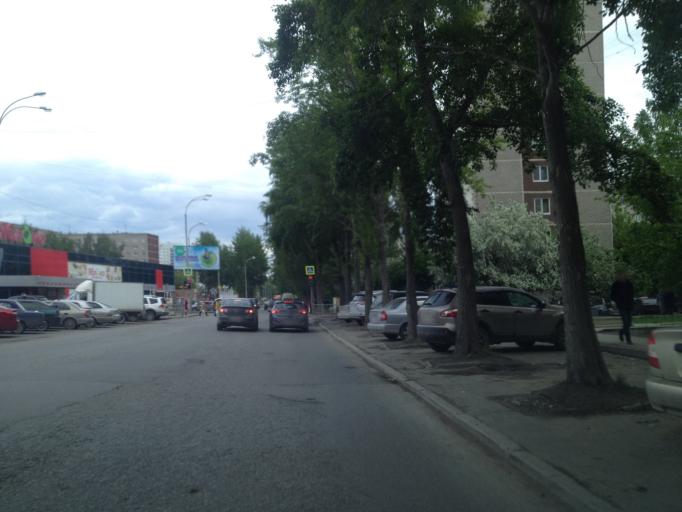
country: RU
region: Sverdlovsk
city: Yekaterinburg
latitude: 56.8692
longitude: 60.5534
